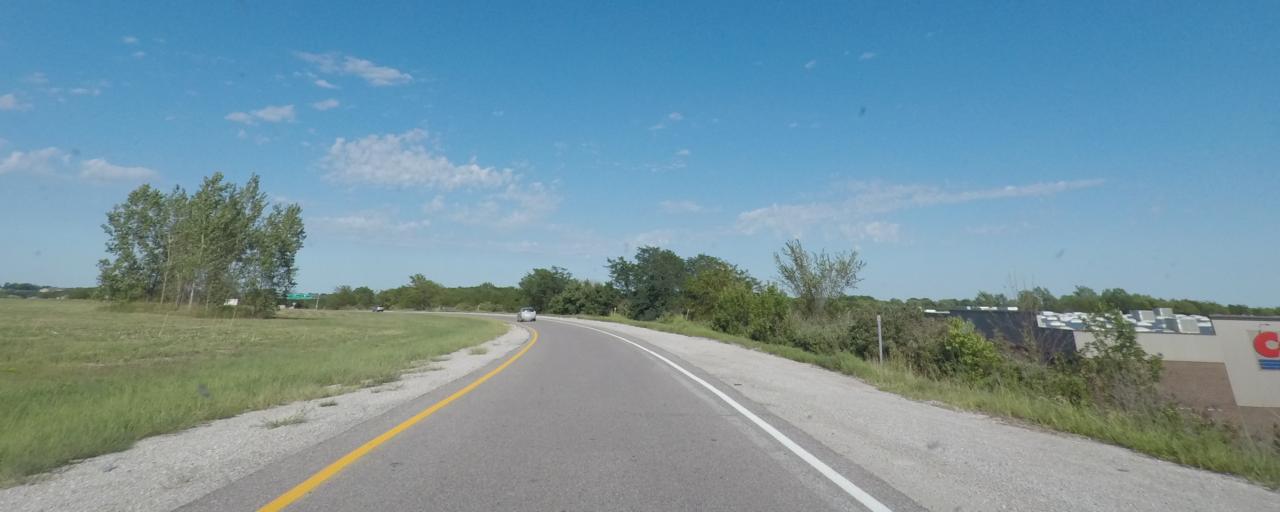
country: US
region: Missouri
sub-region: Clay County
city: Gladstone
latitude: 39.2557
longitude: -94.6002
